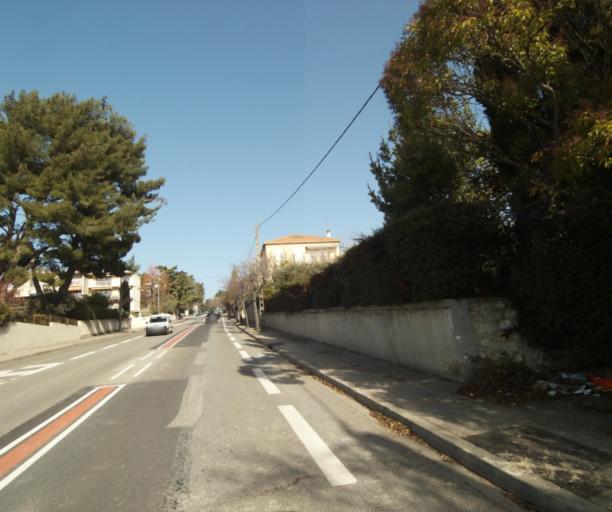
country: FR
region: Provence-Alpes-Cote d'Azur
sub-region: Departement des Bouches-du-Rhone
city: Aix-en-Provence
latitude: 43.5401
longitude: 5.4424
